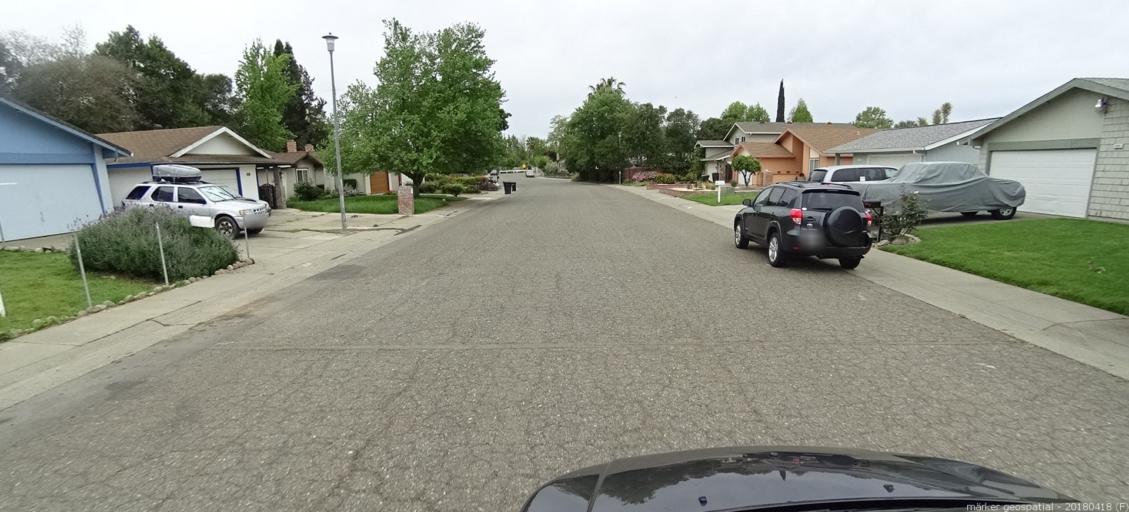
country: US
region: California
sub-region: Sacramento County
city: La Riviera
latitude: 38.5687
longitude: -121.3505
